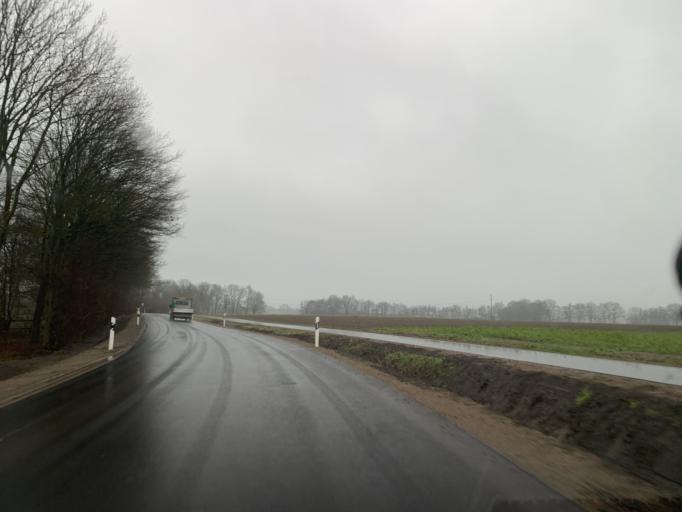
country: DE
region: North Rhine-Westphalia
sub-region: Regierungsbezirk Munster
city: Nottuln
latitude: 51.9191
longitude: 7.4057
